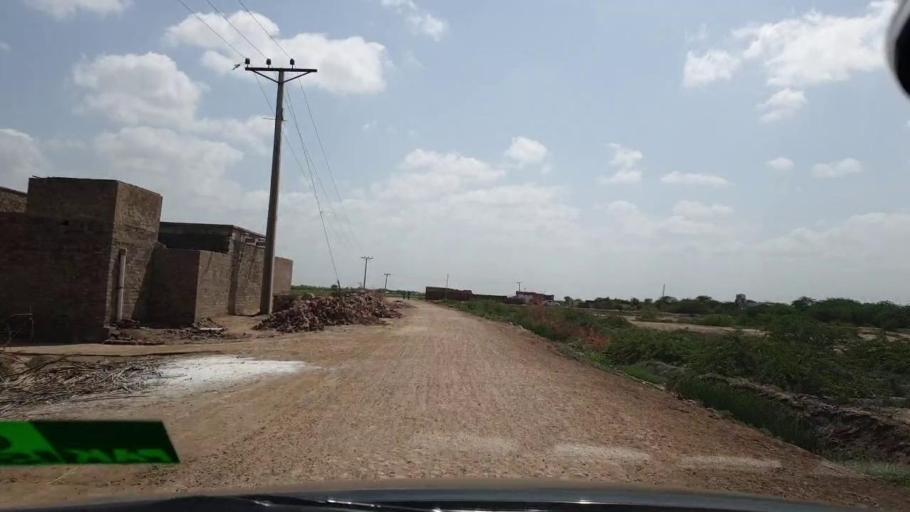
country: PK
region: Sindh
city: Kadhan
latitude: 24.6162
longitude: 69.1855
